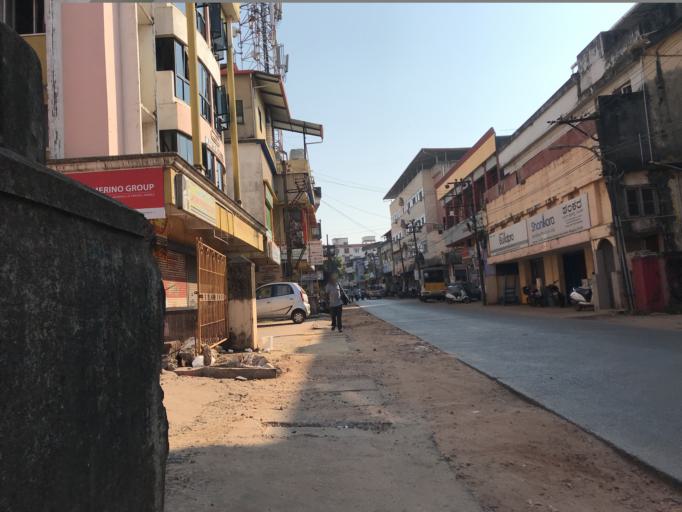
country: IN
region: Karnataka
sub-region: Dakshina Kannada
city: Mangalore
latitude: 12.8689
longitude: 74.8333
